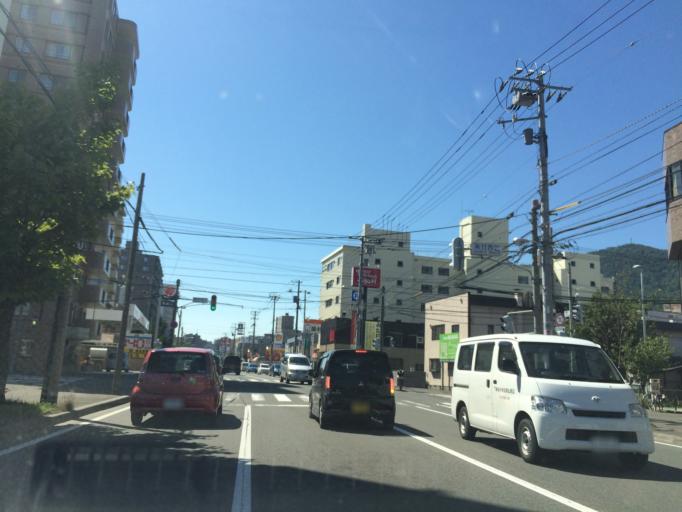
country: JP
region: Hokkaido
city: Sapporo
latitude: 43.0434
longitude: 141.3253
